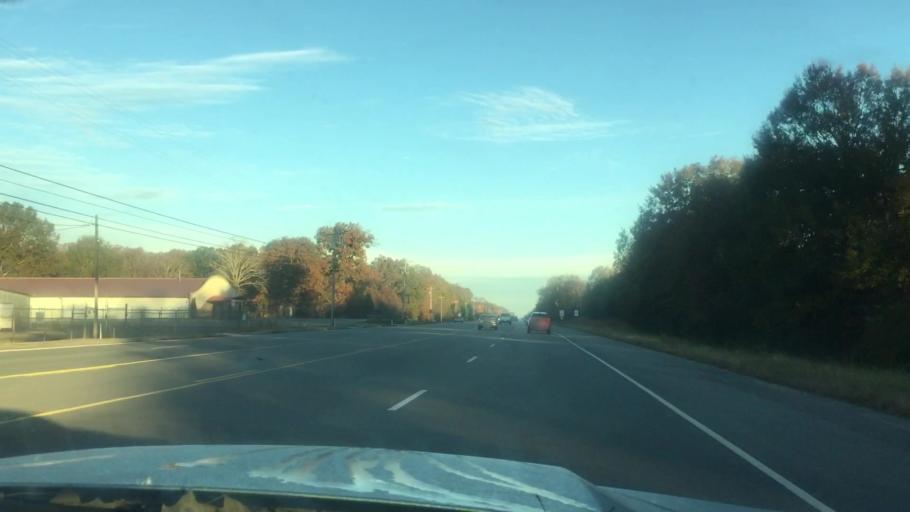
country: US
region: Tennessee
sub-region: Franklin County
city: Estill Springs
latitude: 35.2928
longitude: -86.1473
